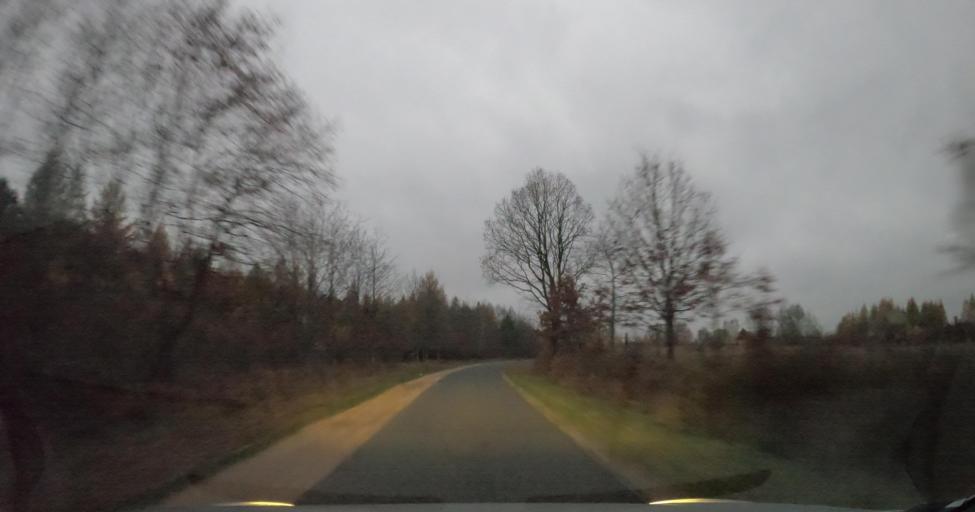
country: PL
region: West Pomeranian Voivodeship
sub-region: Powiat bialogardzki
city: Tychowo
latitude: 53.8628
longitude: 16.2320
